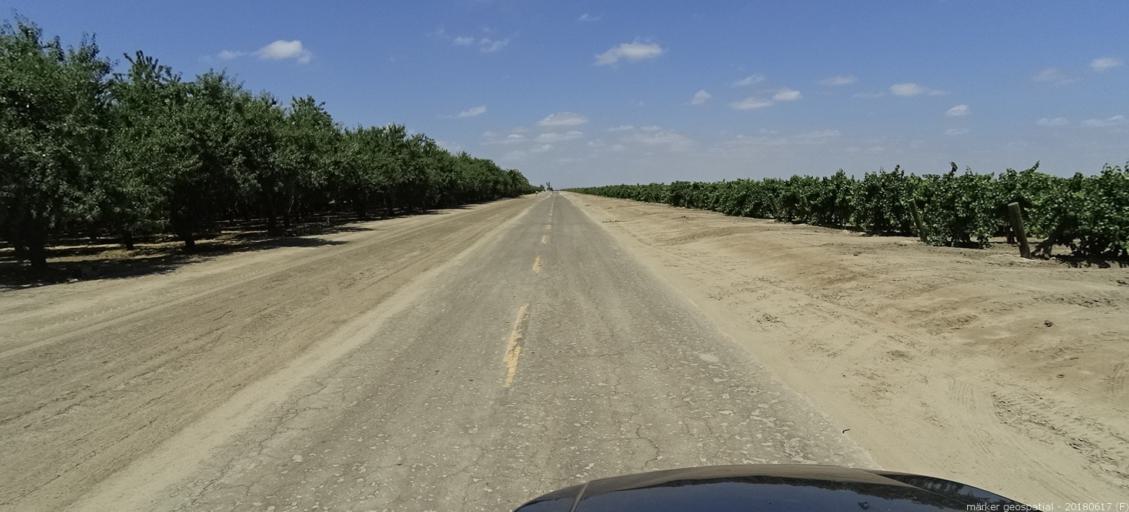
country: US
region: California
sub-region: Fresno County
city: Biola
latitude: 36.8241
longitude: -120.1329
